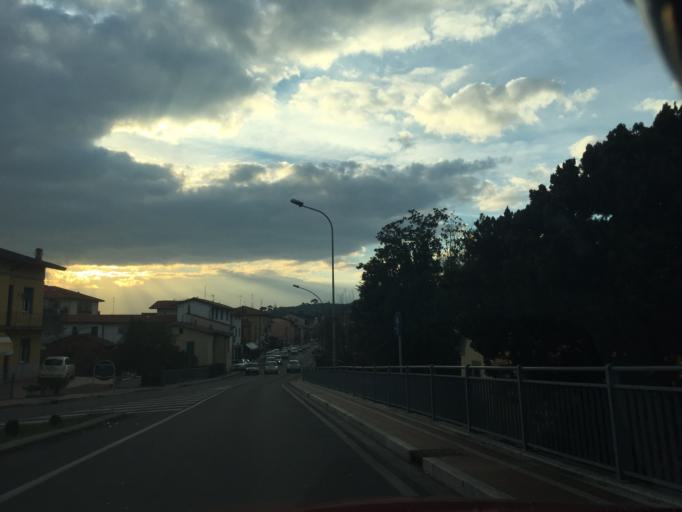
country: IT
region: Tuscany
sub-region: Provincia di Pistoia
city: Margine Coperta-Traversagna
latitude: 43.8865
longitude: 10.7594
